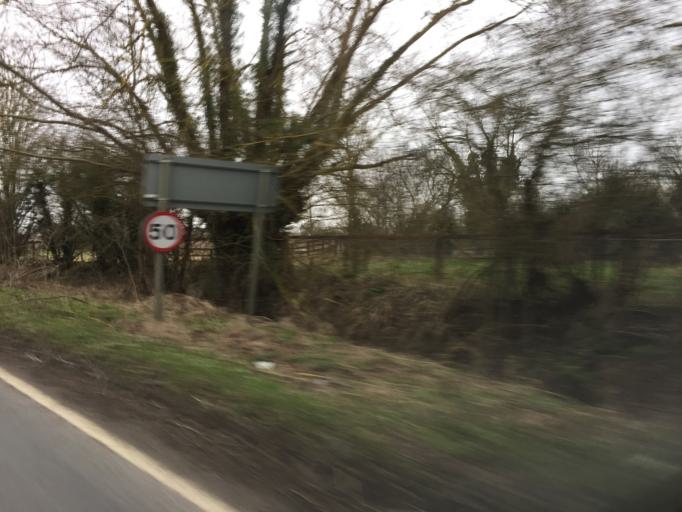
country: GB
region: England
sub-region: Oxfordshire
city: Stanford in the Vale
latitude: 51.6214
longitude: -1.4984
